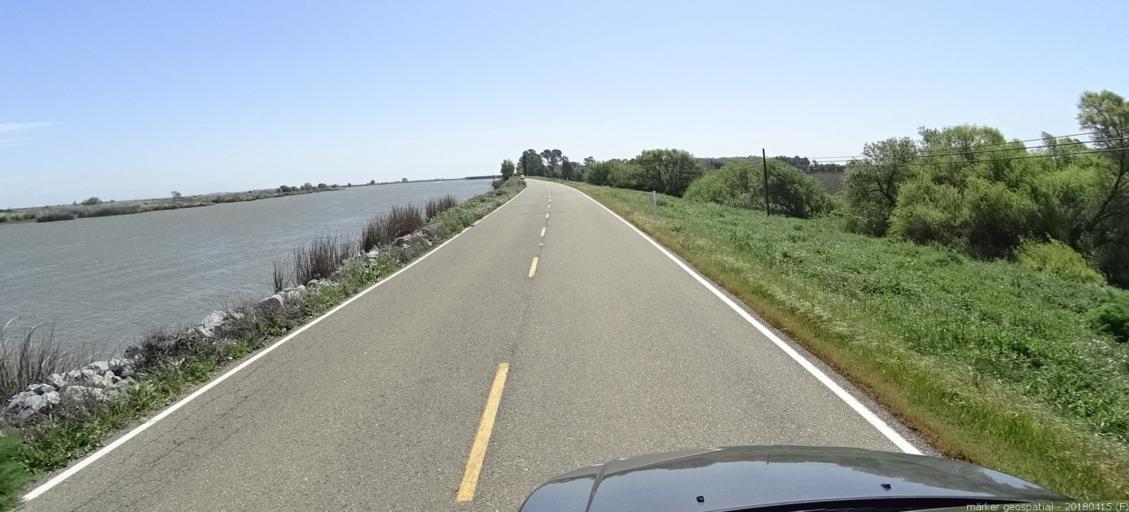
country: US
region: California
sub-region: Contra Costa County
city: Bethel Island
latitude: 38.1098
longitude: -121.5814
